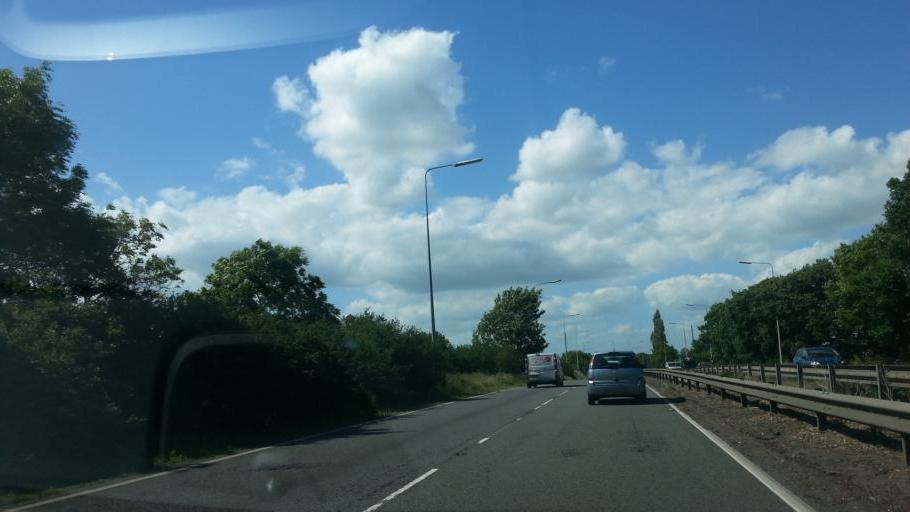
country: GB
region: England
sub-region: Central Bedfordshire
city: Astwick
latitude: 52.0325
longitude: -0.2168
